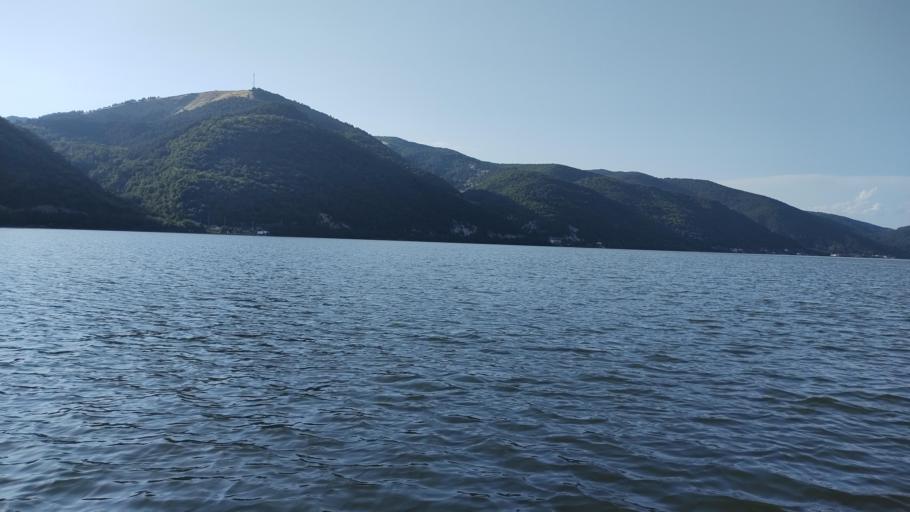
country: RO
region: Mehedinti
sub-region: Comuna Dubova
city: Dubova
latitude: 44.5477
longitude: 22.2251
